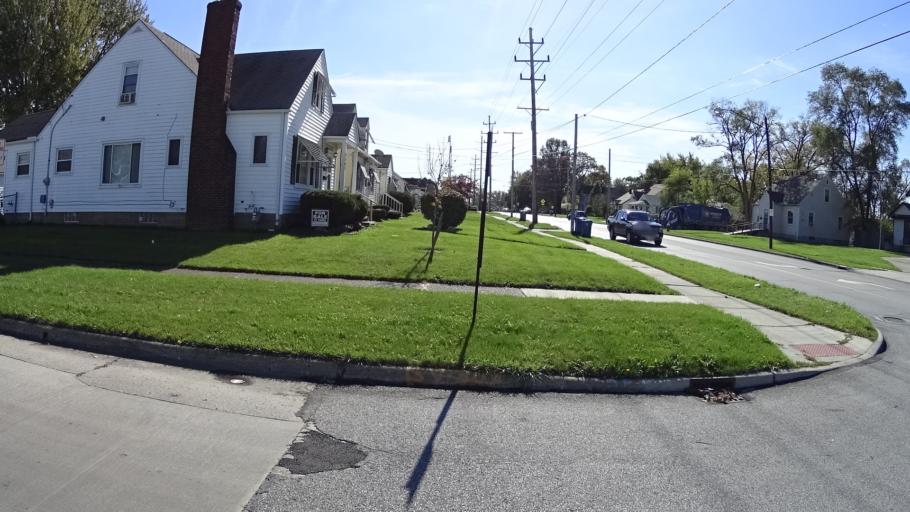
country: US
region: Ohio
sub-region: Lorain County
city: Lorain
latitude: 41.4487
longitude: -82.1850
